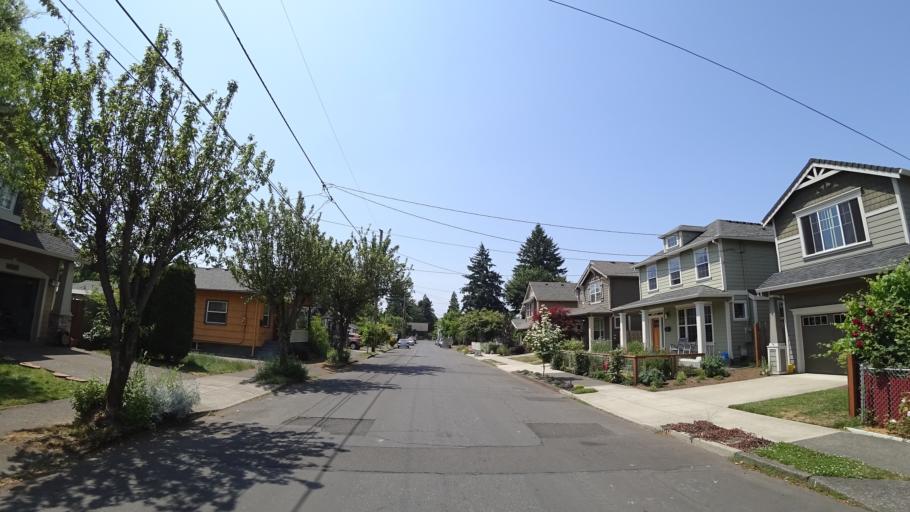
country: US
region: Oregon
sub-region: Multnomah County
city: Portland
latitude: 45.5845
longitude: -122.6957
